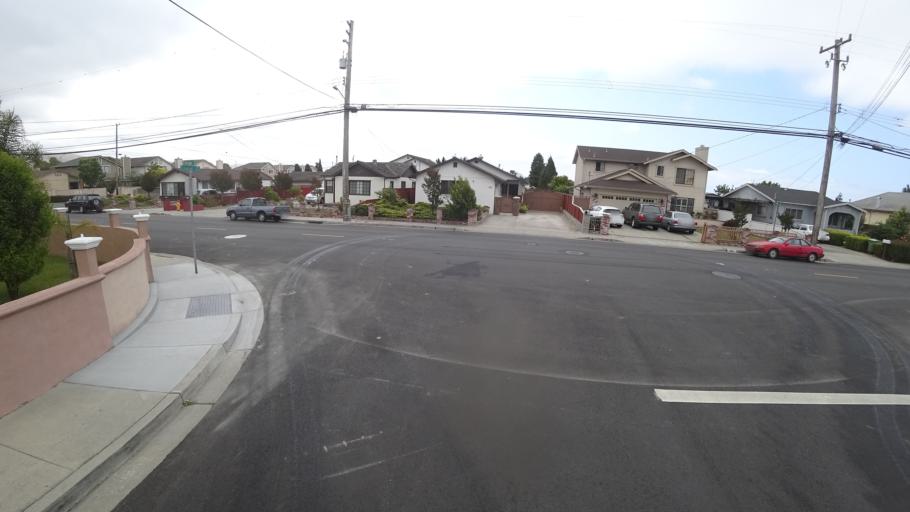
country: US
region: California
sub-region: Alameda County
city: Hayward
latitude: 37.6262
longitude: -122.0638
